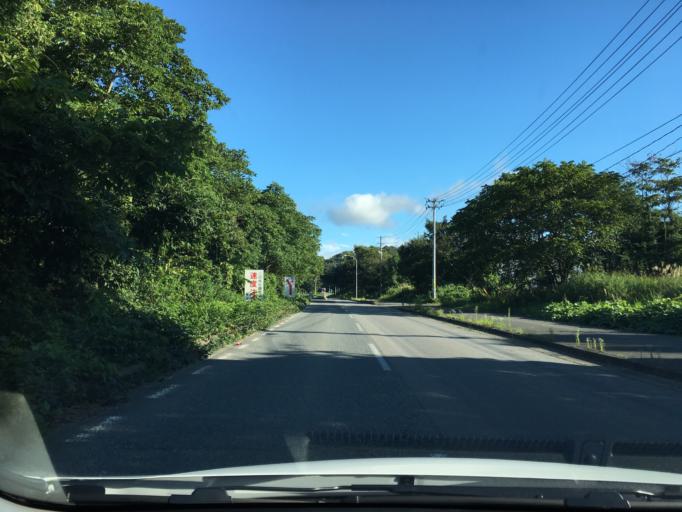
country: JP
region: Yamagata
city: Yonezawa
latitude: 37.9151
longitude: 140.1605
